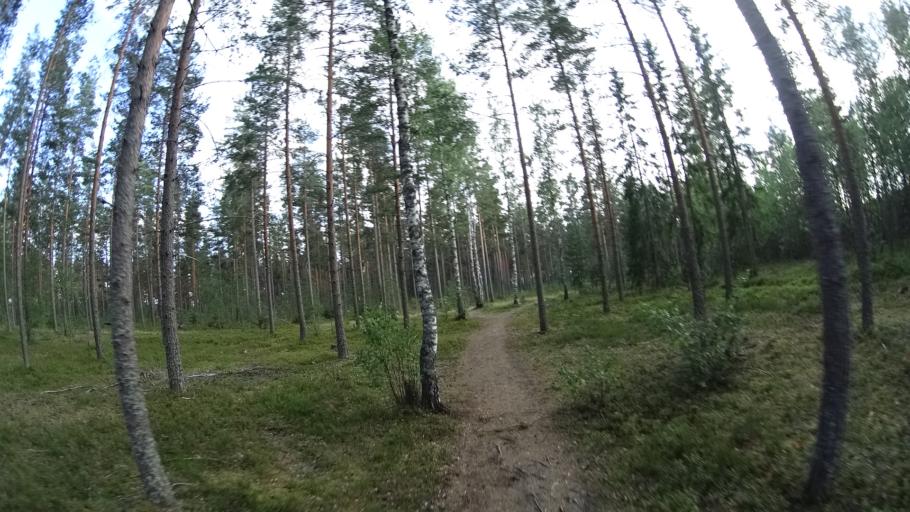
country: FI
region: Uusimaa
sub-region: Helsinki
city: Vihti
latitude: 60.3305
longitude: 24.2912
